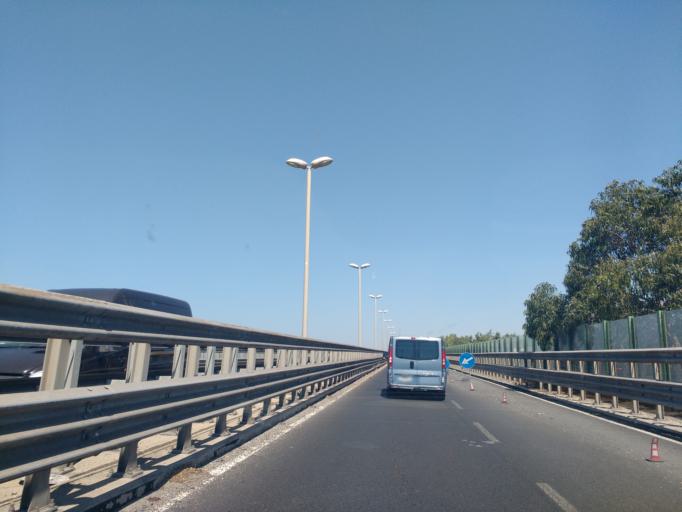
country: IT
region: Latium
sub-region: Citta metropolitana di Roma Capitale
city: Fiumicino-Isola Sacra
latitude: 41.7724
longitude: 12.2565
